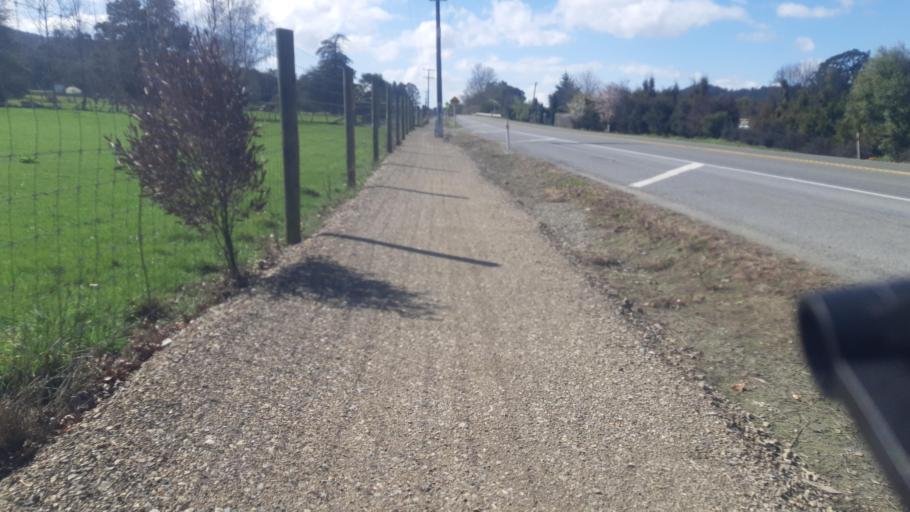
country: NZ
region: Tasman
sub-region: Tasman District
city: Wakefield
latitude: -41.4488
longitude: 172.9602
